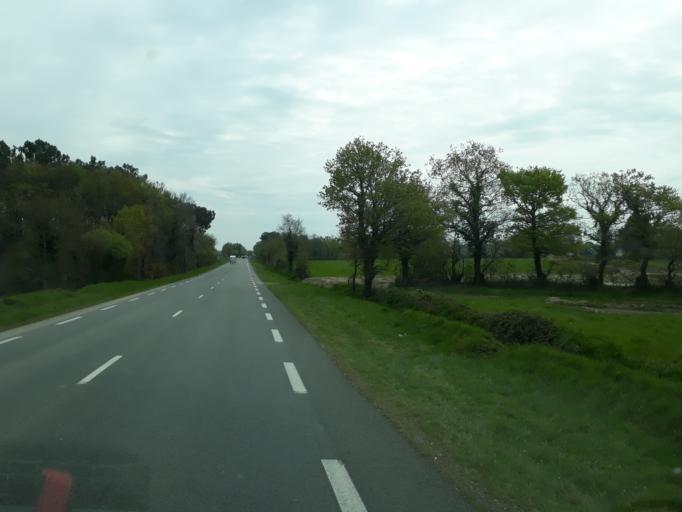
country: FR
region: Brittany
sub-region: Departement du Morbihan
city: Ferel
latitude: 47.5236
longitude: -2.3779
